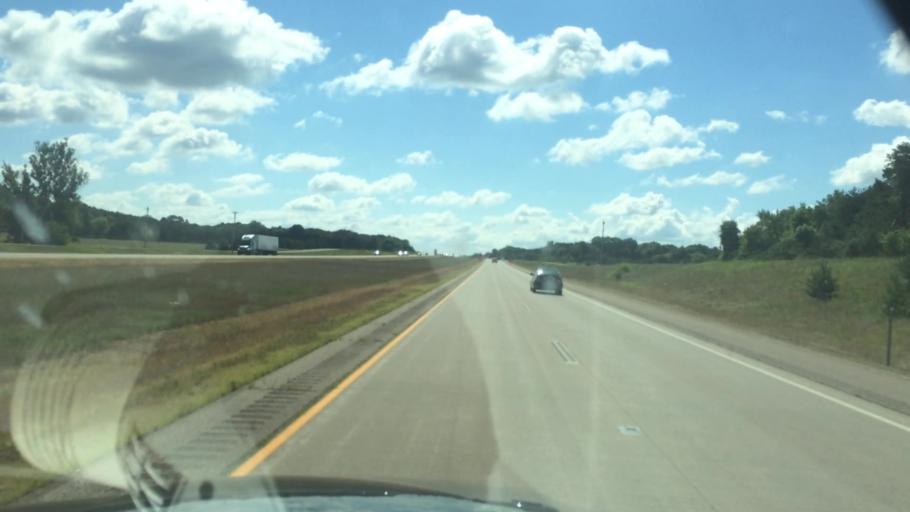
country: US
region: Wisconsin
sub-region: Waupaca County
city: King
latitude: 44.3700
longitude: -89.1494
